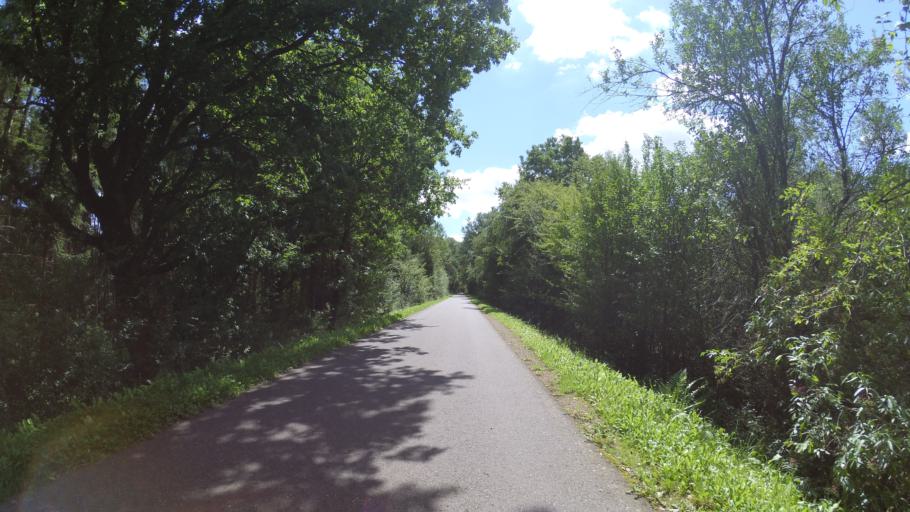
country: DE
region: Saarland
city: Sankt Wendel
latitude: 49.4828
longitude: 7.1575
